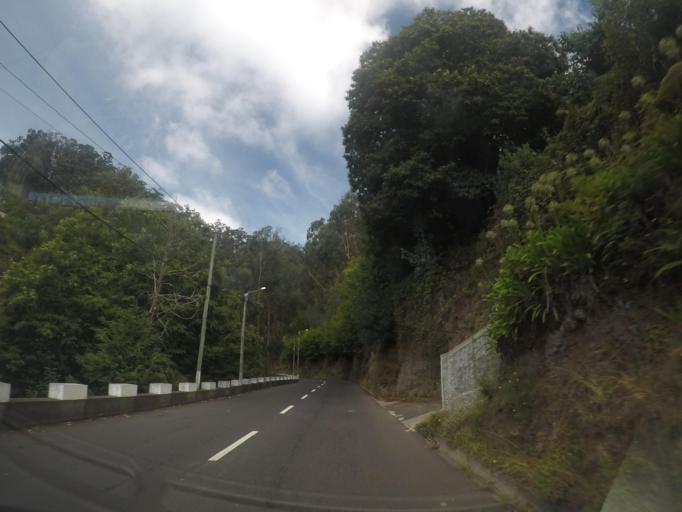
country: PT
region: Madeira
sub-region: Camara de Lobos
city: Curral das Freiras
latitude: 32.6890
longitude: -16.9514
